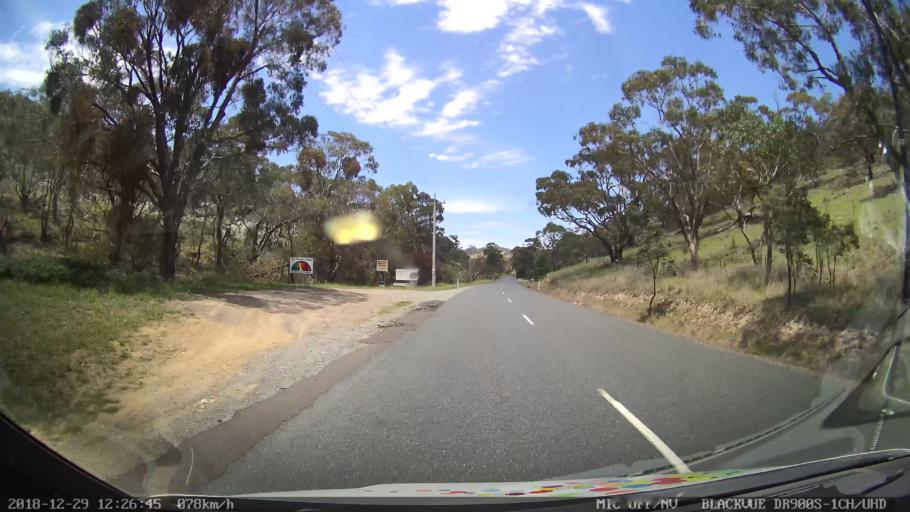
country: AU
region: Australian Capital Territory
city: Macarthur
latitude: -35.4689
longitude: 149.2241
